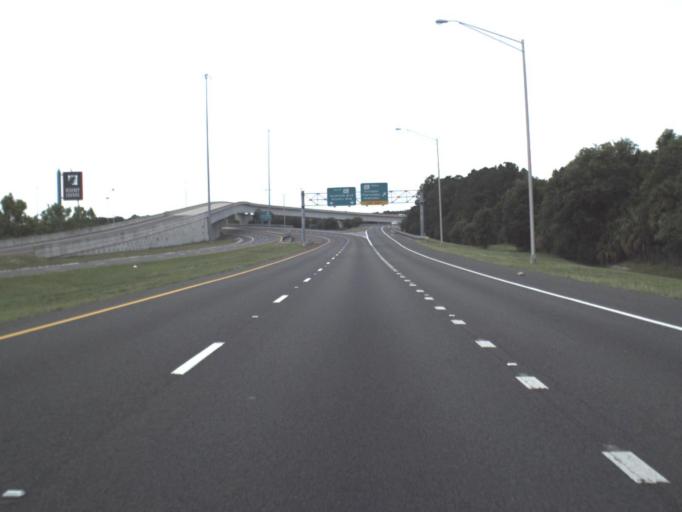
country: US
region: Florida
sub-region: Duval County
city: Jacksonville
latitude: 30.3271
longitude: -81.5566
